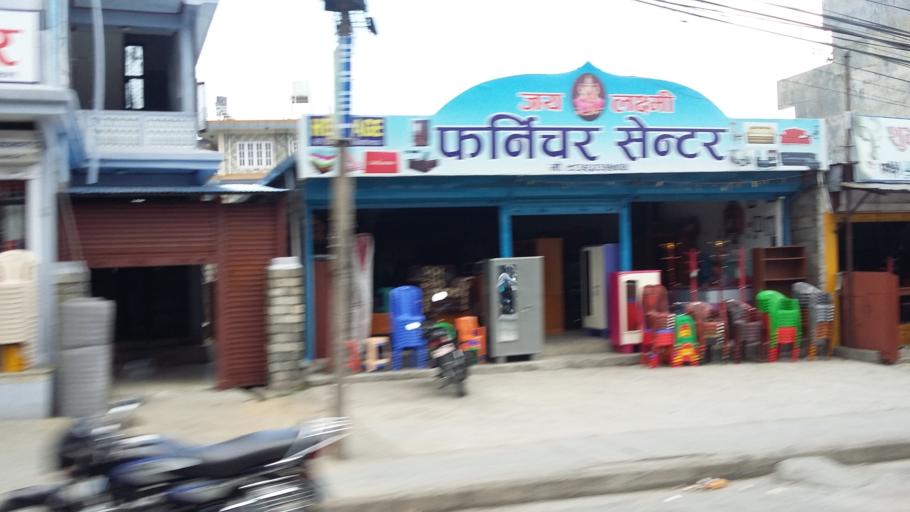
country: NP
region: Western Region
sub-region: Gandaki Zone
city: Pokhara
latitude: 28.2169
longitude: 83.9863
